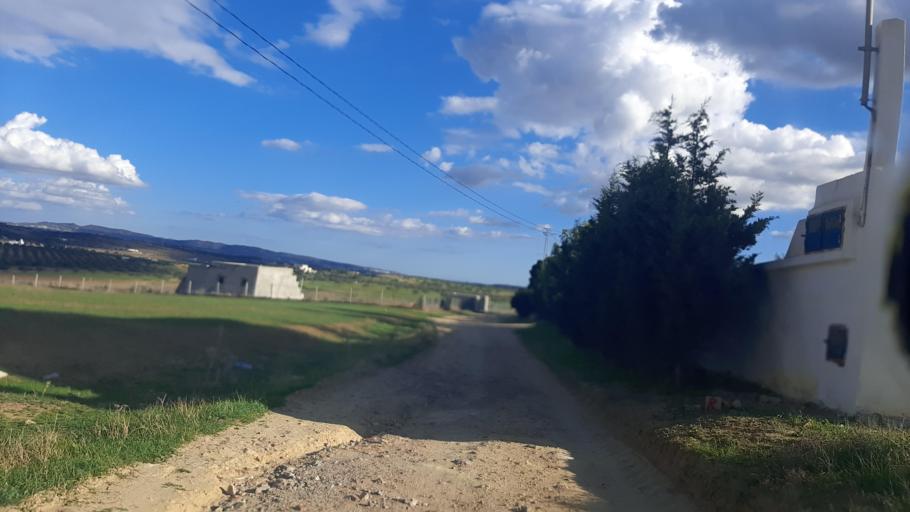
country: TN
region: Nabul
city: Bu `Urqub
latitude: 36.4656
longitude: 10.4816
